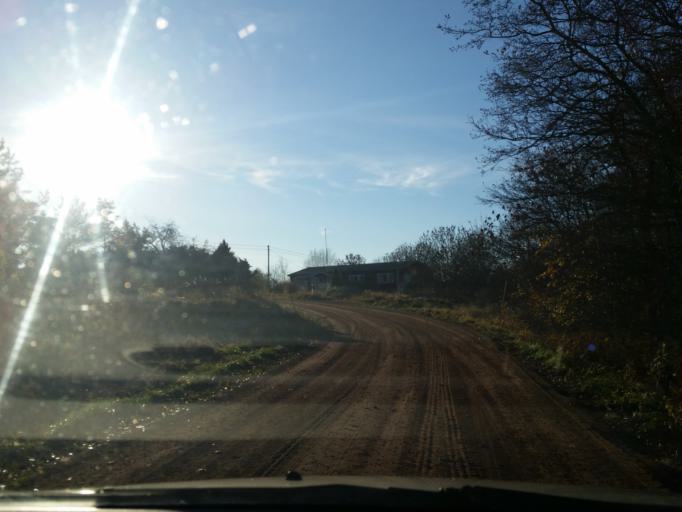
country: AX
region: Alands skaergard
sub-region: Braendoe
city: Braendoe
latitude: 60.4538
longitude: 20.9419
